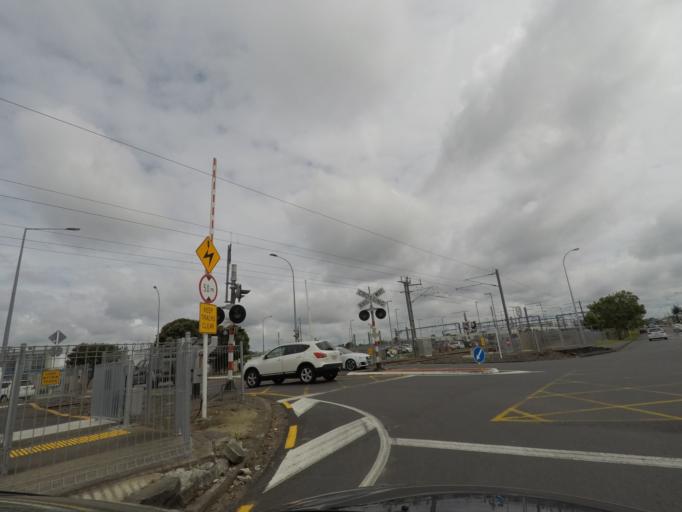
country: NZ
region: Auckland
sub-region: Auckland
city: Waitakere
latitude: -36.8910
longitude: 174.6317
